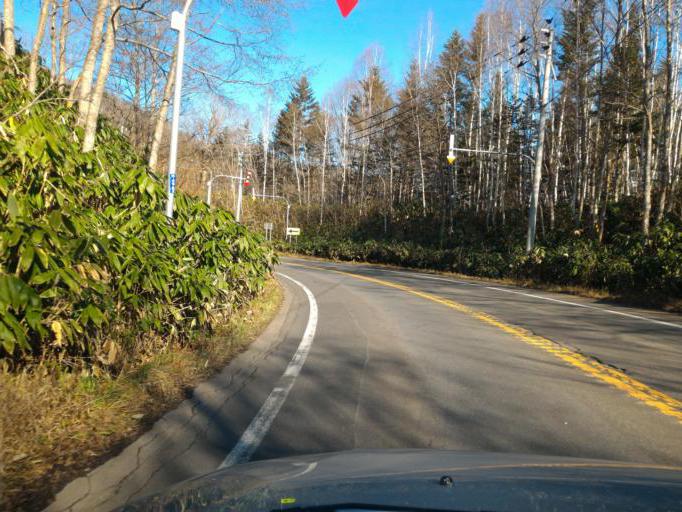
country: JP
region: Hokkaido
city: Bibai
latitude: 43.2609
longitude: 142.0300
